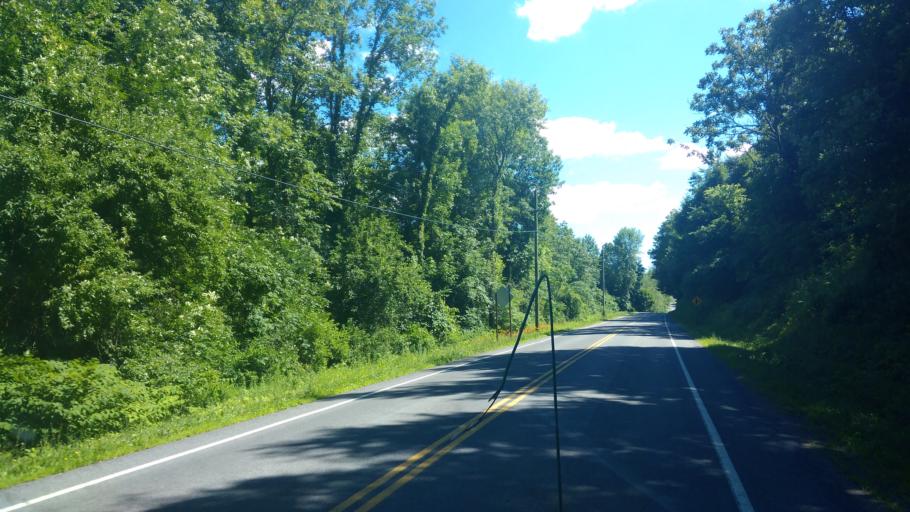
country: US
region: New York
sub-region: Wayne County
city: Sodus
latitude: 43.1700
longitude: -77.0130
